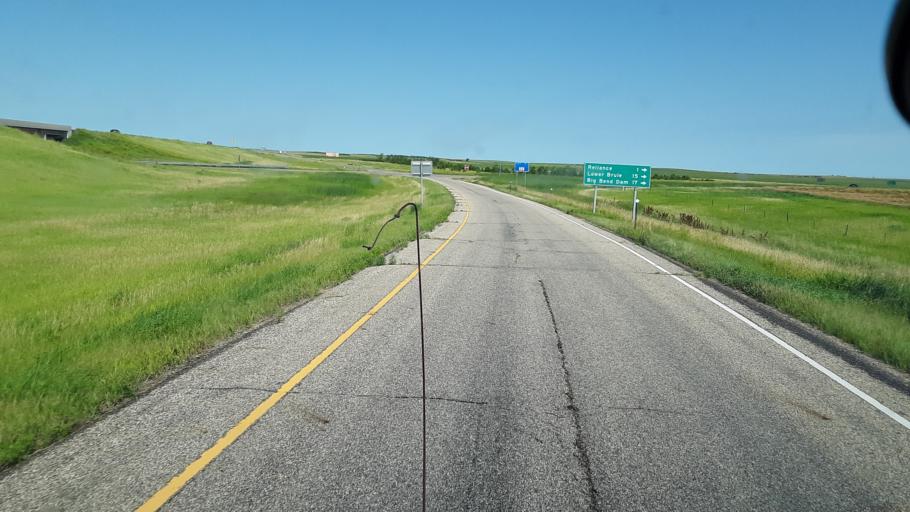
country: US
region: South Dakota
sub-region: Lyman County
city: Kennebec
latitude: 43.8644
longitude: -99.6040
